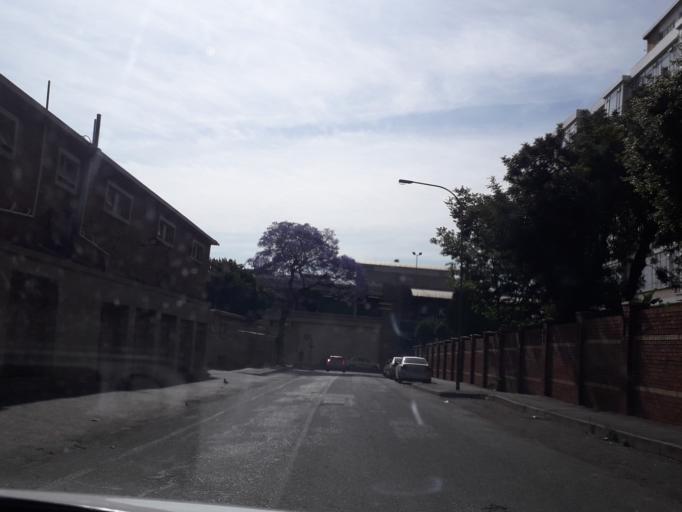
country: ZA
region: Gauteng
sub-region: City of Johannesburg Metropolitan Municipality
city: Johannesburg
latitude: -26.1659
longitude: 28.0521
